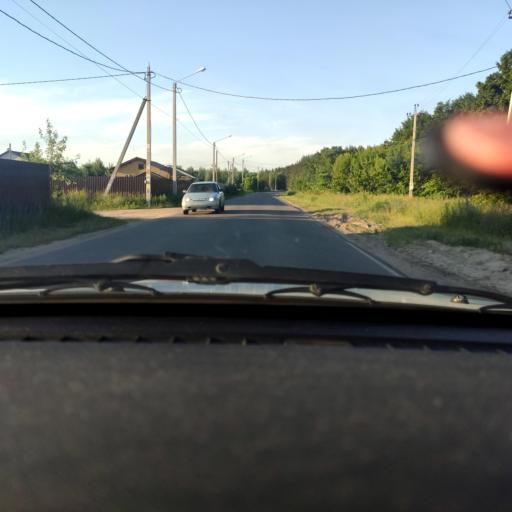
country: RU
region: Voronezj
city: Ramon'
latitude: 51.8902
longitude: 39.2713
